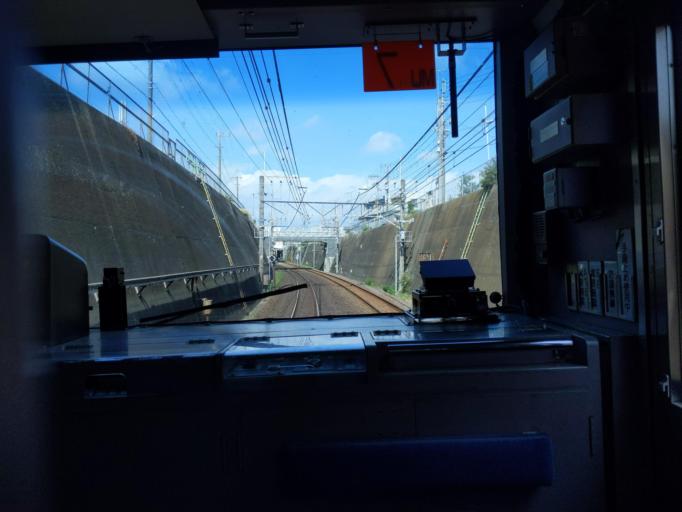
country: JP
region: Chiba
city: Funabashi
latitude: 35.7279
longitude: 139.9680
